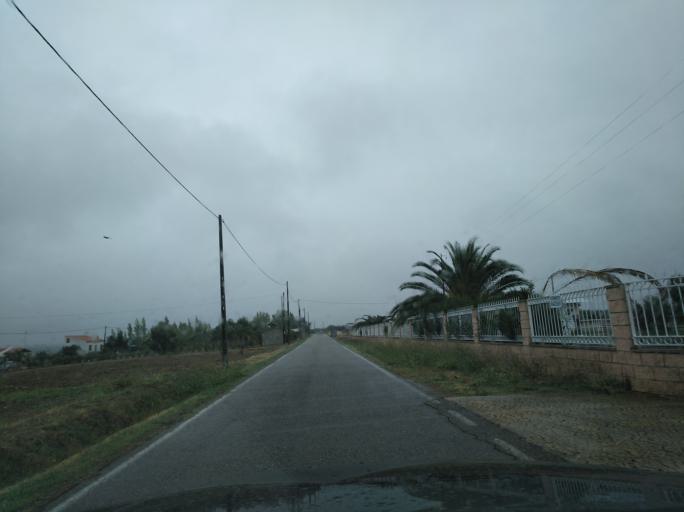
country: PT
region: Portalegre
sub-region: Campo Maior
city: Campo Maior
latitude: 38.9574
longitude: -7.0822
